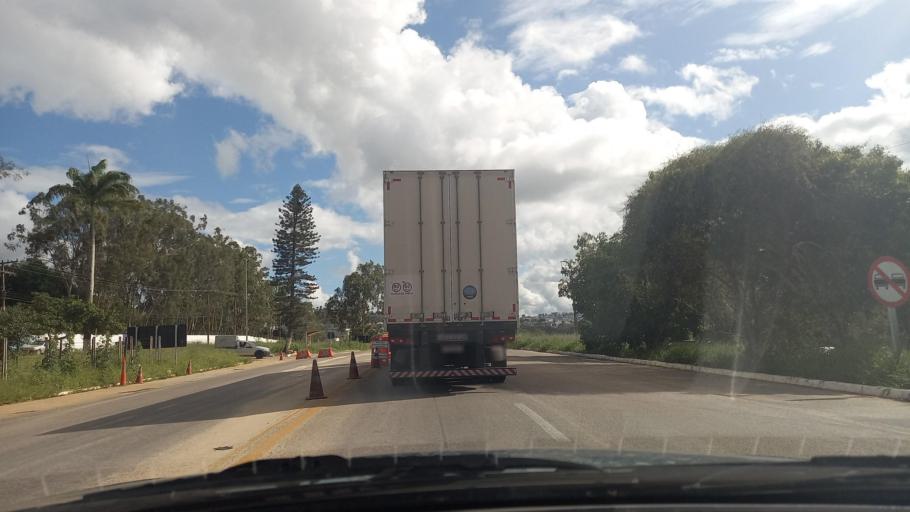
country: BR
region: Pernambuco
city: Garanhuns
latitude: -8.8697
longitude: -36.4632
